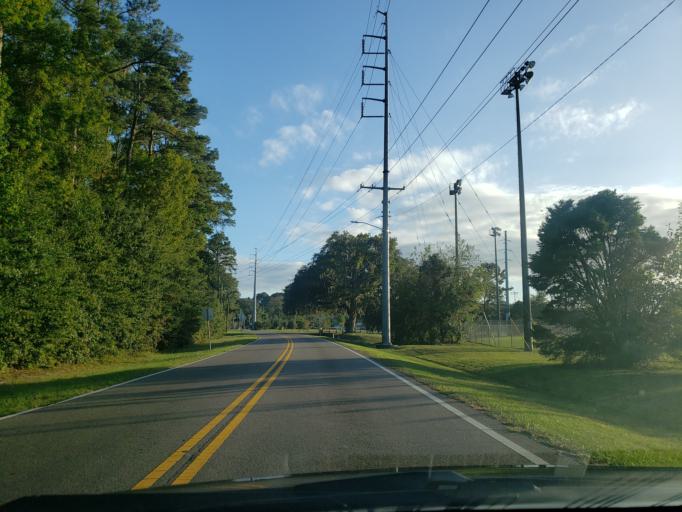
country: US
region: Georgia
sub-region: Chatham County
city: Isle of Hope
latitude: 31.9958
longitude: -81.0784
